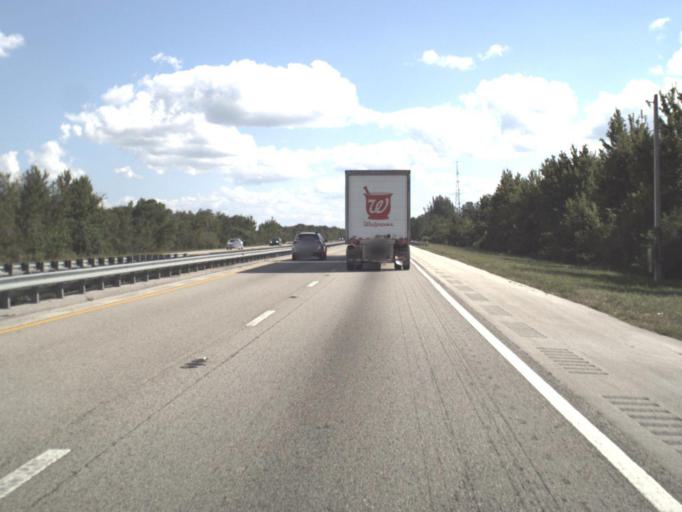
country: US
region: Florida
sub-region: Brevard County
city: June Park
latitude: 27.8766
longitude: -81.0239
